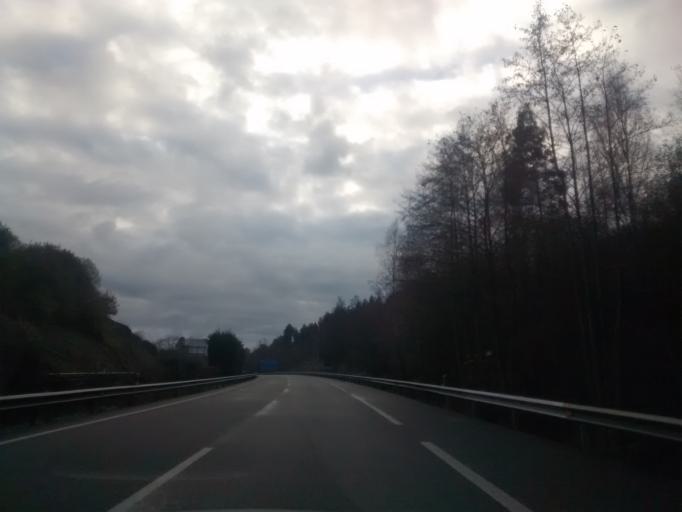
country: ES
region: Cantabria
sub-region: Provincia de Cantabria
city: Colindres
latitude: 43.3936
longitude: -3.4813
